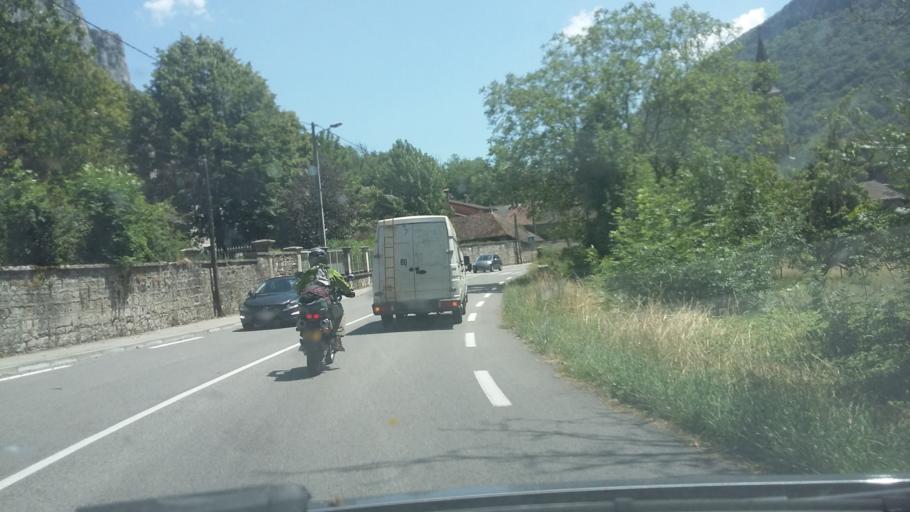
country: FR
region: Rhone-Alpes
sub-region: Departement de l'Ain
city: Tenay
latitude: 45.8467
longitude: 5.5596
